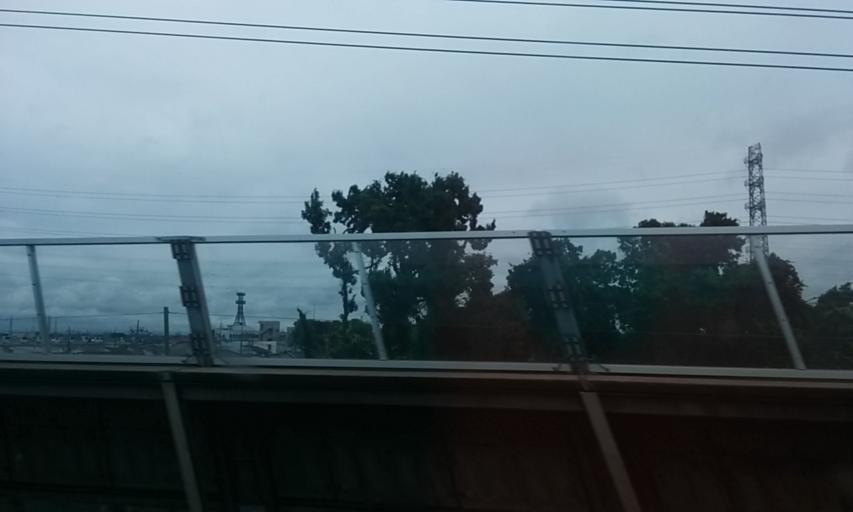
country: JP
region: Tochigi
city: Oyama
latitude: 36.2916
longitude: 139.7900
